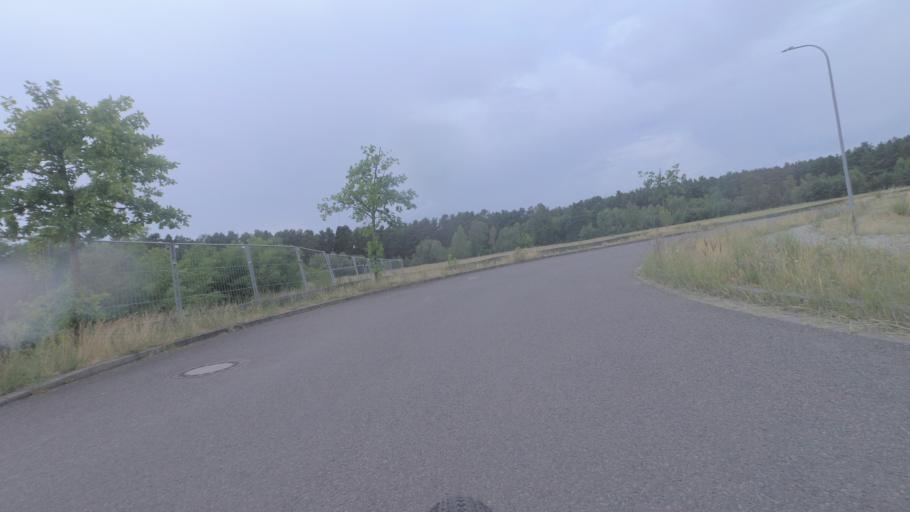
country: DE
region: Brandenburg
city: Ludwigsfelde
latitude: 52.3208
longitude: 13.2503
